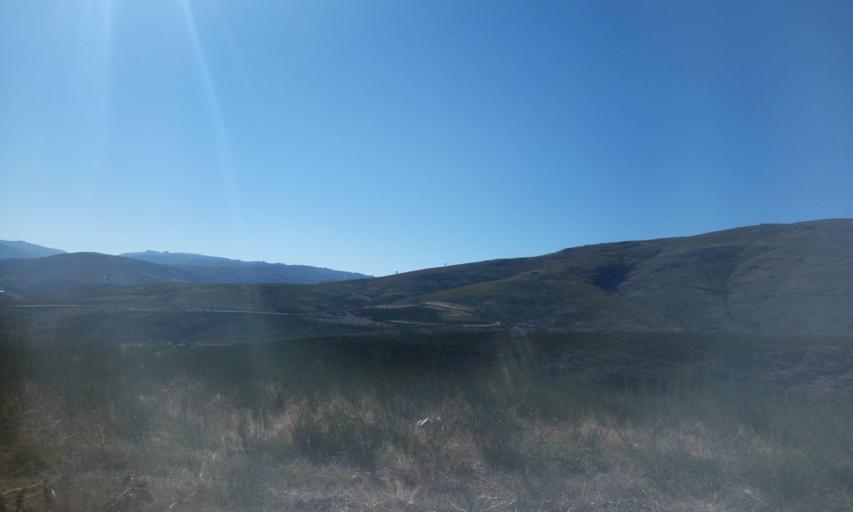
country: PT
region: Guarda
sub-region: Manteigas
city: Manteigas
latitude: 40.4708
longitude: -7.5045
